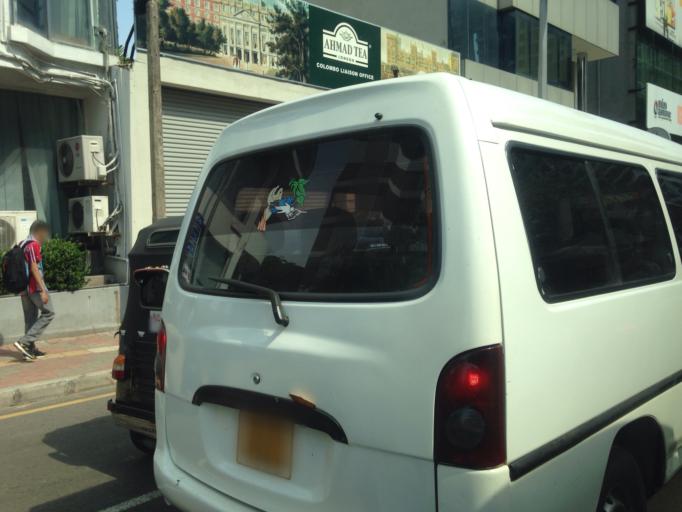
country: LK
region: Western
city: Colombo
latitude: 6.9075
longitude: 79.8532
